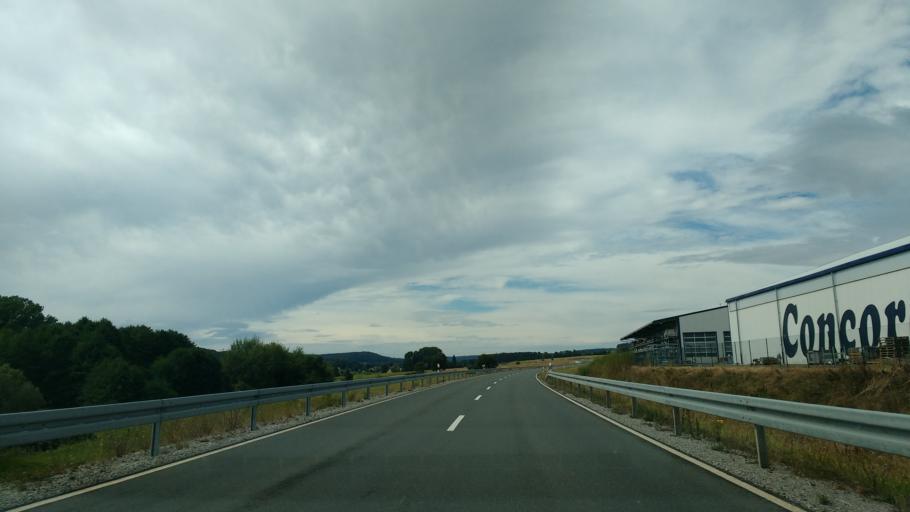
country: DE
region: Bavaria
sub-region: Regierungsbezirk Mittelfranken
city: Burghaslach
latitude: 49.7661
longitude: 10.5620
